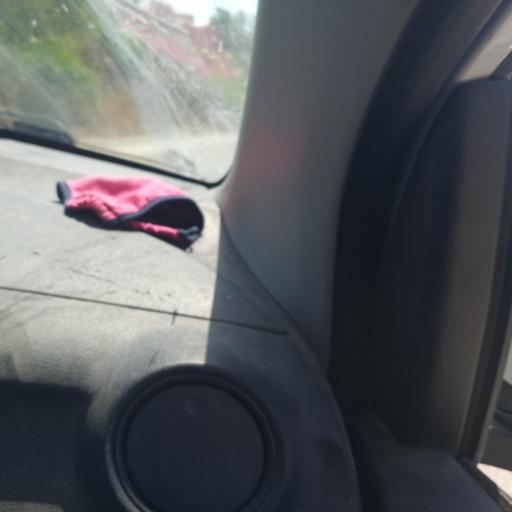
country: TN
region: Nabul
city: Qulaybiyah
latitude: 36.8600
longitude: 11.0446
